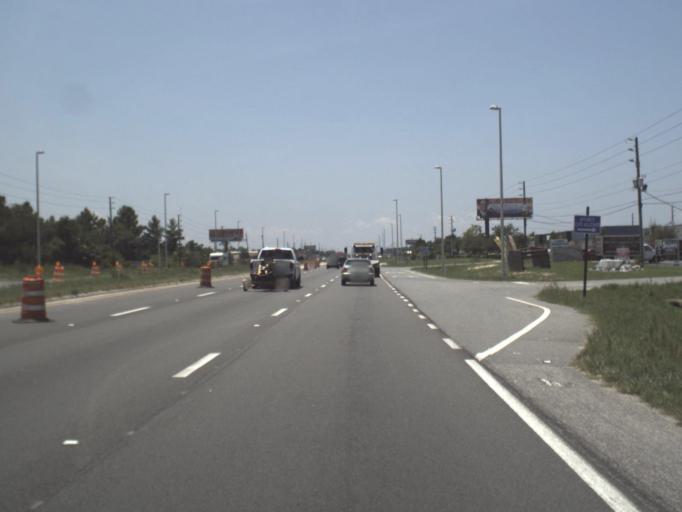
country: US
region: Florida
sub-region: Pasco County
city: Hudson
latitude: 28.3993
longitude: -82.6603
